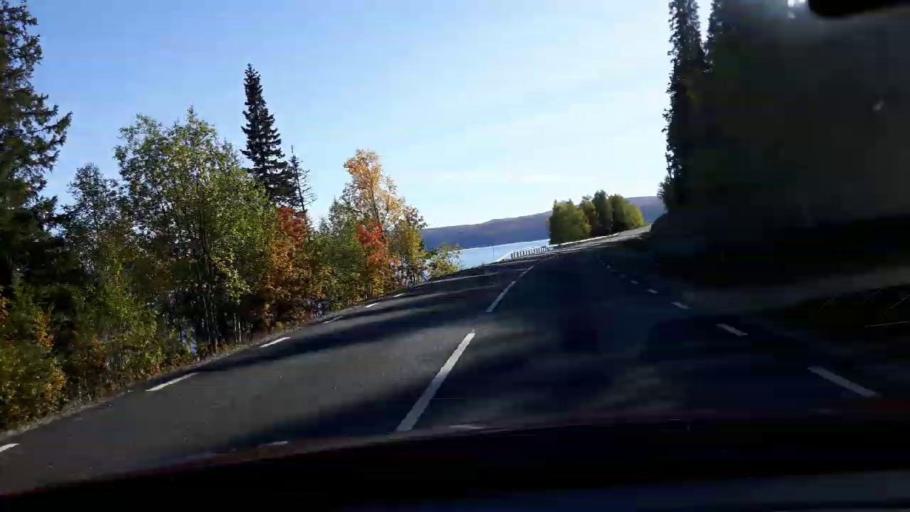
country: NO
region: Nord-Trondelag
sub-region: Royrvik
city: Royrvik
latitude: 64.8307
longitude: 14.0789
